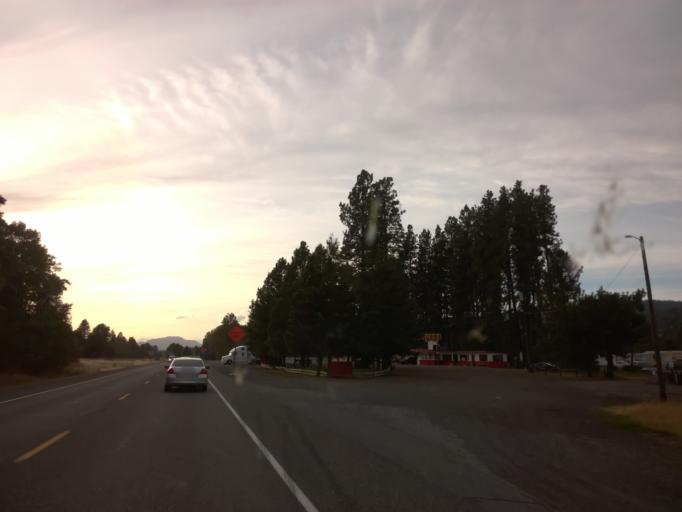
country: US
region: Washington
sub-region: Kittitas County
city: Cle Elum
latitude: 47.1844
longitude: -120.8897
